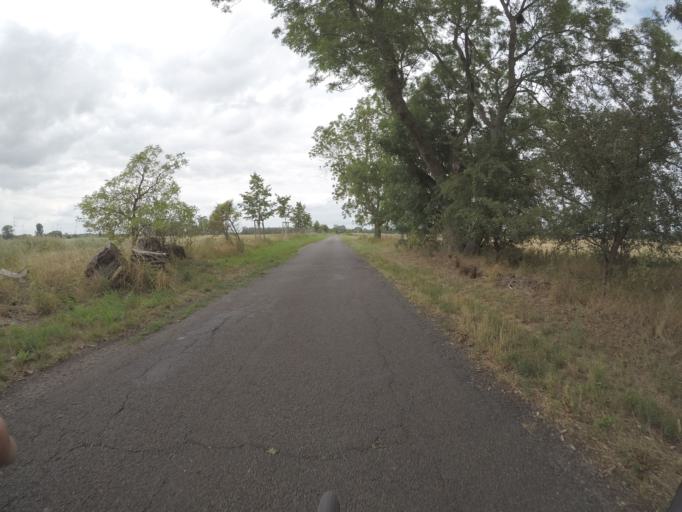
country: DE
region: Brandenburg
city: Wustermark
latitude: 52.6046
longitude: 12.9384
